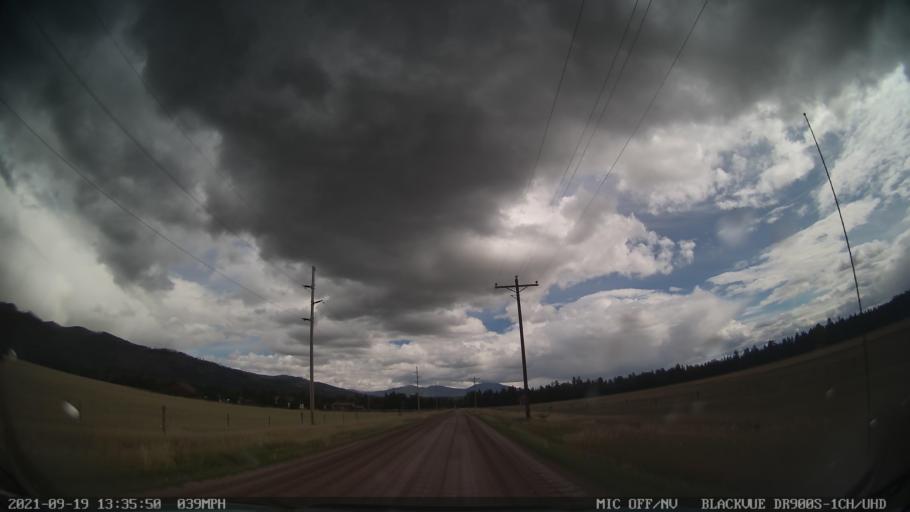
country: US
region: Montana
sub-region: Missoula County
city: Seeley Lake
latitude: 47.1066
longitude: -113.3064
